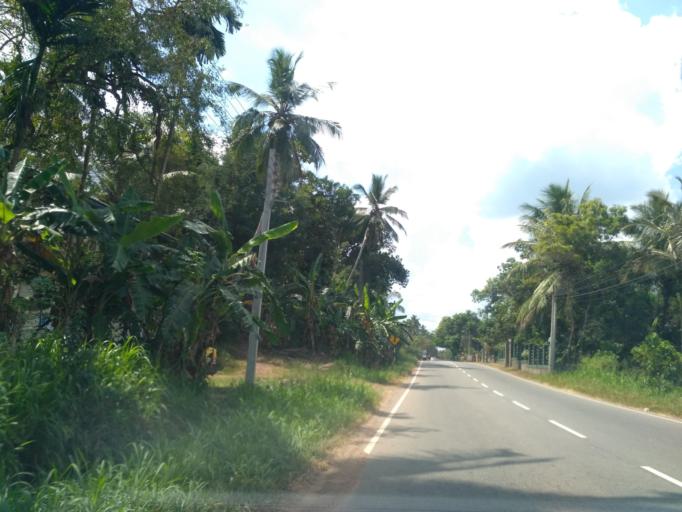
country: LK
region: North Western
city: Kuliyapitiya
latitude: 7.3270
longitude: 80.0549
